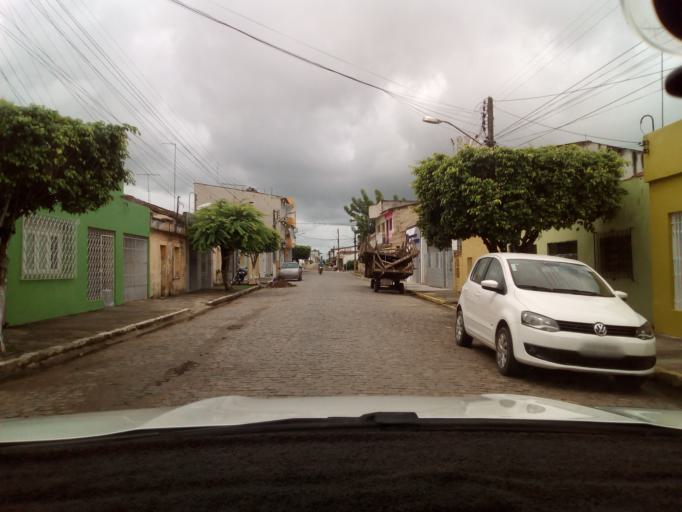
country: BR
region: Paraiba
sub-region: Pedras De Fogo
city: Pedras de Fogo
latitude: -7.4063
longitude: -35.1156
